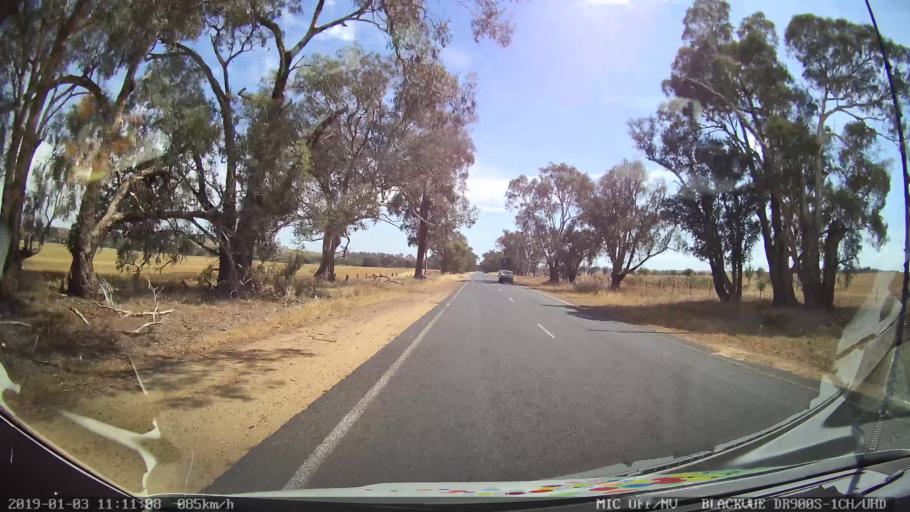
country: AU
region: New South Wales
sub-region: Young
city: Young
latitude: -34.2185
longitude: 148.2593
